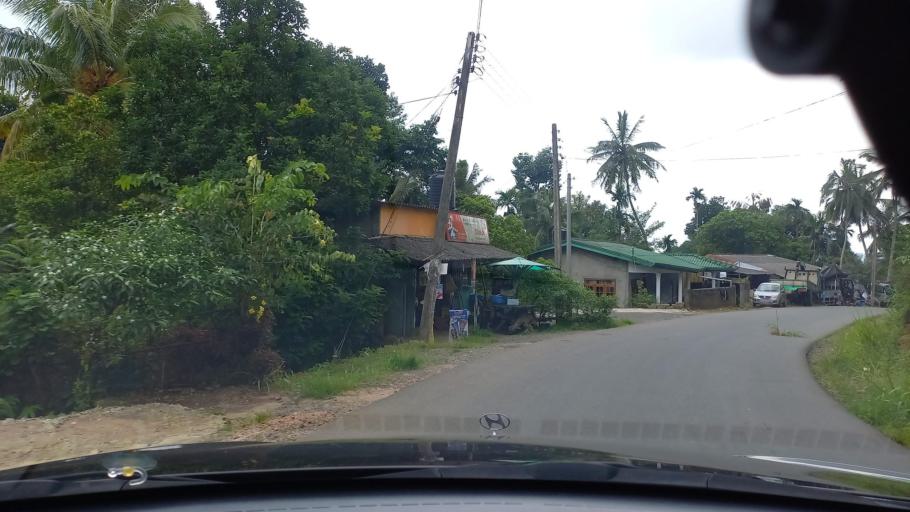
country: LK
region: Central
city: Gampola
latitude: 7.2073
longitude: 80.6222
